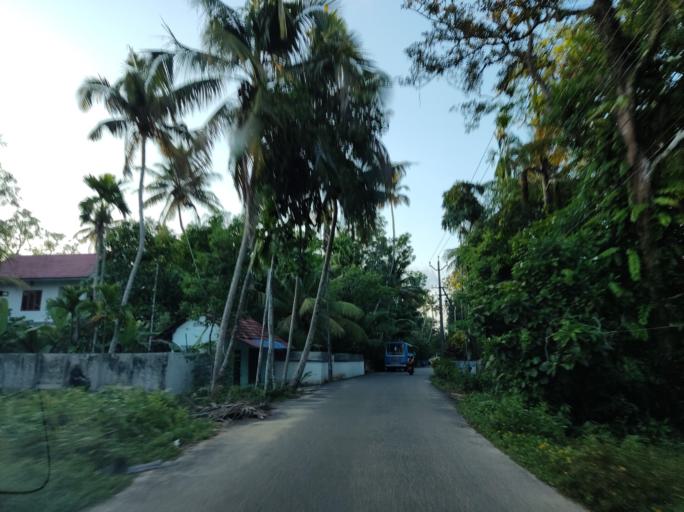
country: IN
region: Kerala
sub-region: Alappuzha
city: Vayalar
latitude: 9.7170
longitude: 76.2970
